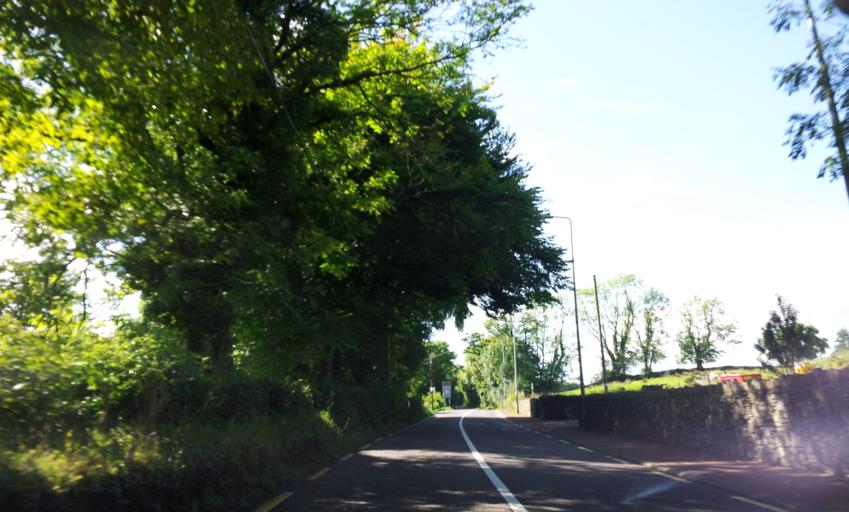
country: IE
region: Munster
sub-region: County Cork
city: Millstreet
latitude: 51.9458
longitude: -9.1735
